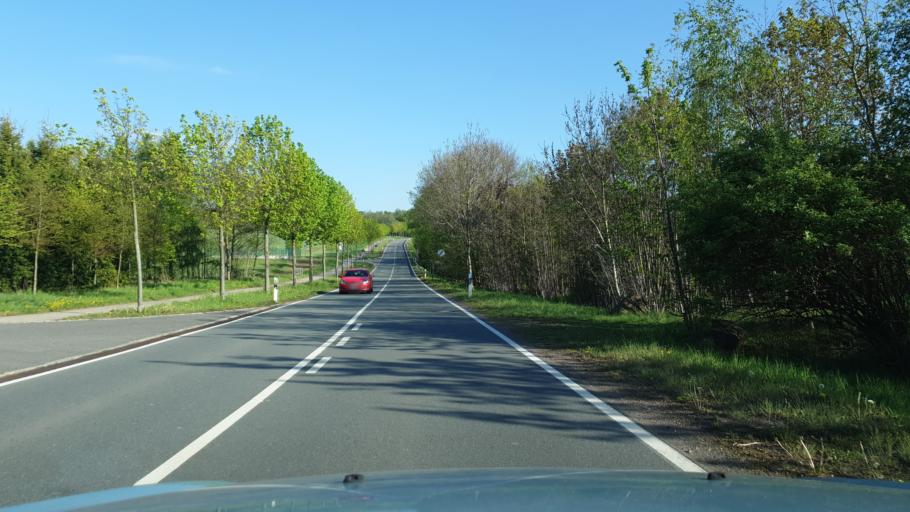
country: DE
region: Saxony
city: Oelsnitz
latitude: 50.7172
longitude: 12.7062
